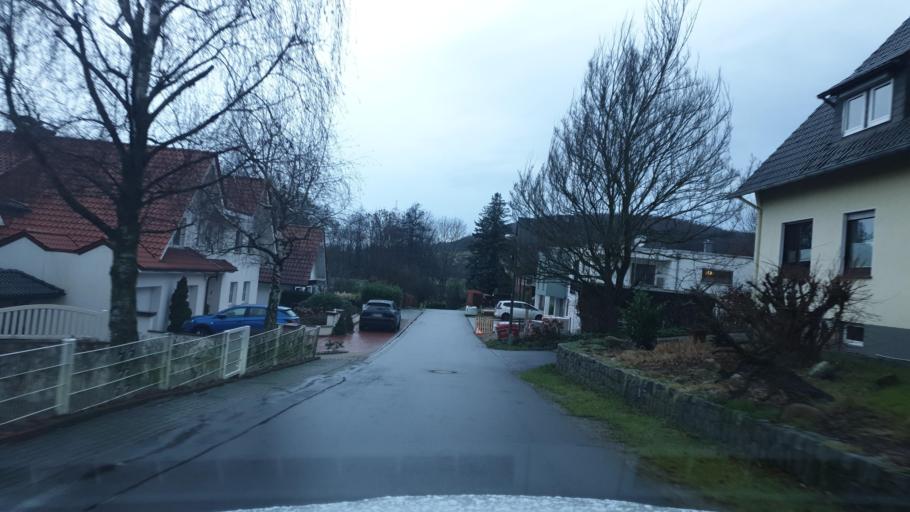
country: DE
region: North Rhine-Westphalia
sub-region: Regierungsbezirk Detmold
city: Hille
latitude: 52.2690
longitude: 8.7576
